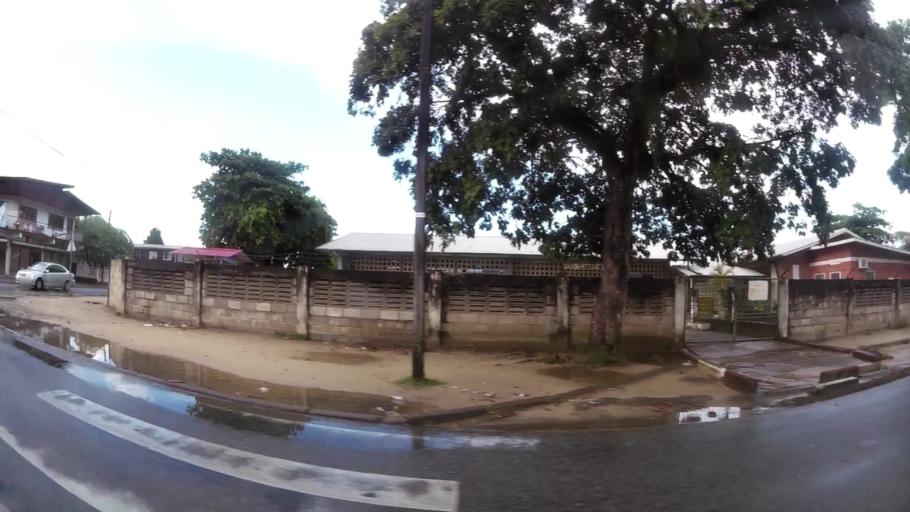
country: SR
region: Paramaribo
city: Paramaribo
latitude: 5.8244
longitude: -55.1818
